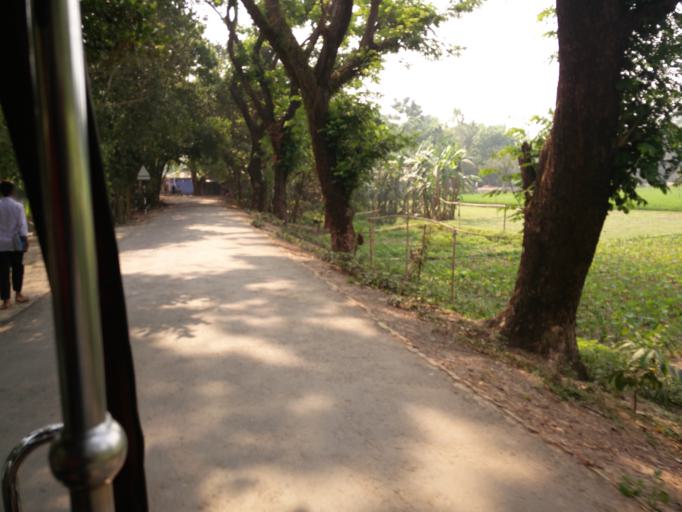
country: BD
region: Dhaka
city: Muktagacha
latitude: 24.9079
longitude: 90.2091
